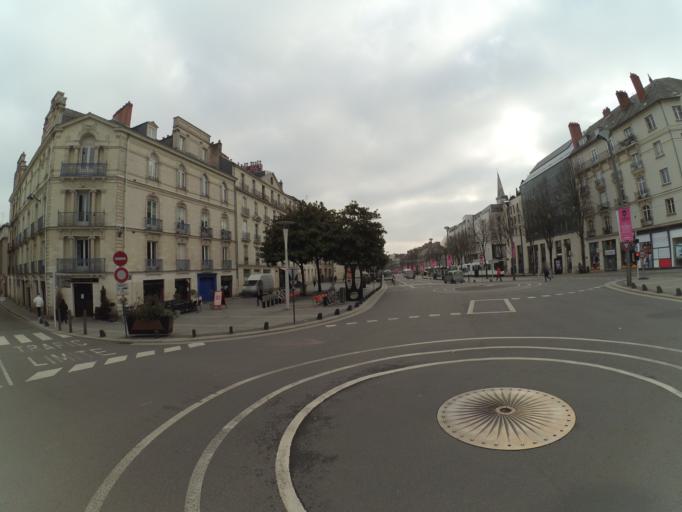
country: FR
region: Pays de la Loire
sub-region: Departement de la Loire-Atlantique
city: Nantes
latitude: 47.2178
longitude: -1.5571
